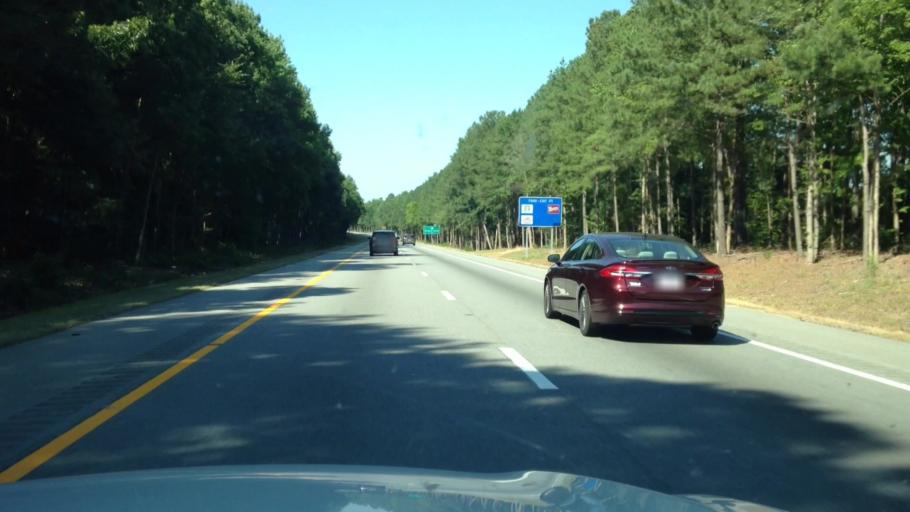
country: US
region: North Carolina
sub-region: Halifax County
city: Weldon
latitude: 36.3813
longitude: -77.6570
